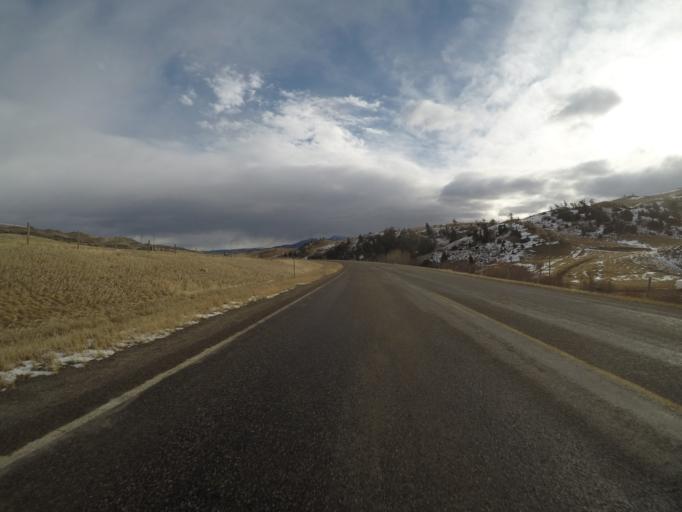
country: US
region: Montana
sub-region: Park County
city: Livingston
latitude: 45.6532
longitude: -110.5952
